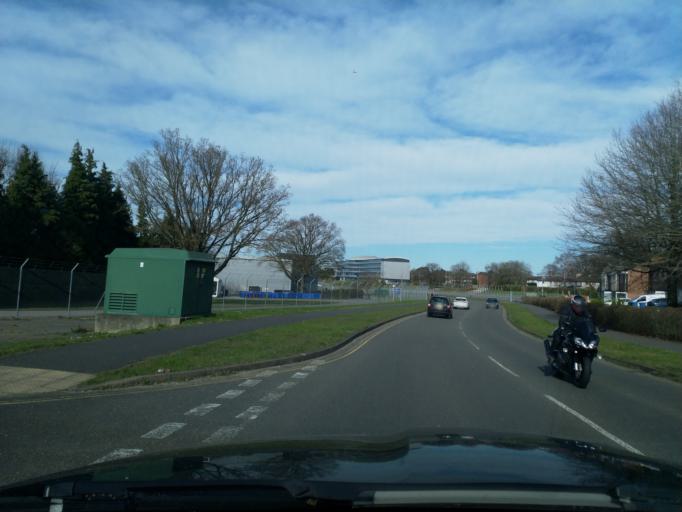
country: GB
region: England
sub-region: Hampshire
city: Farnborough
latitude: 51.2763
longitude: -0.7580
